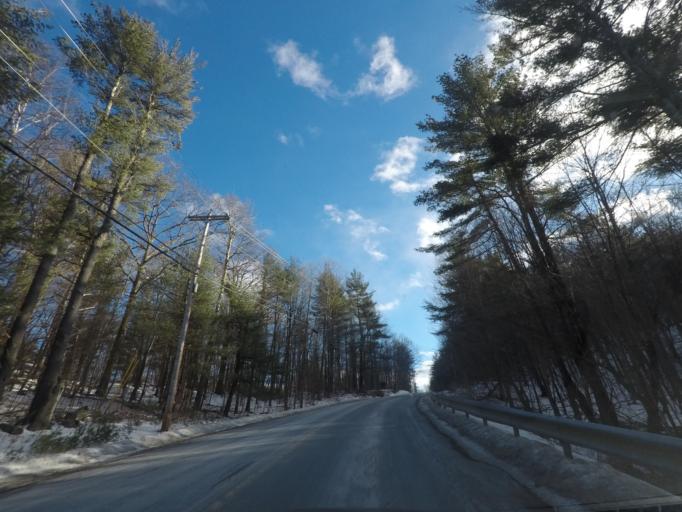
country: US
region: New York
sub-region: Rensselaer County
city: Hoosick Falls
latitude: 42.8254
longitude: -73.3891
